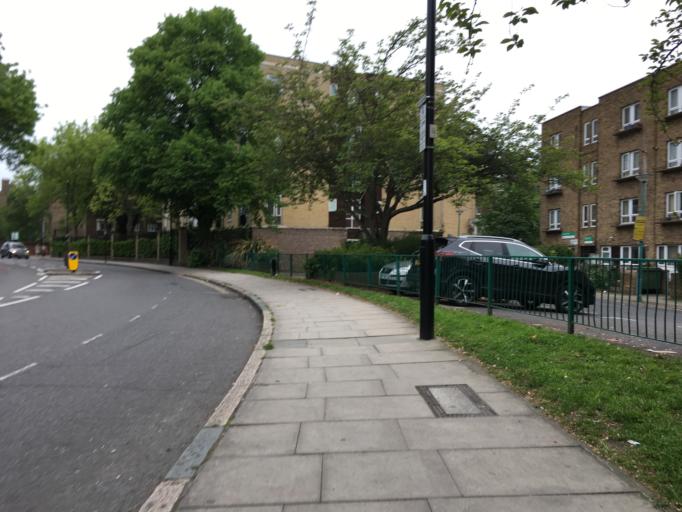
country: GB
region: England
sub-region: Greater London
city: Holloway
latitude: 51.5512
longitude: -0.1307
